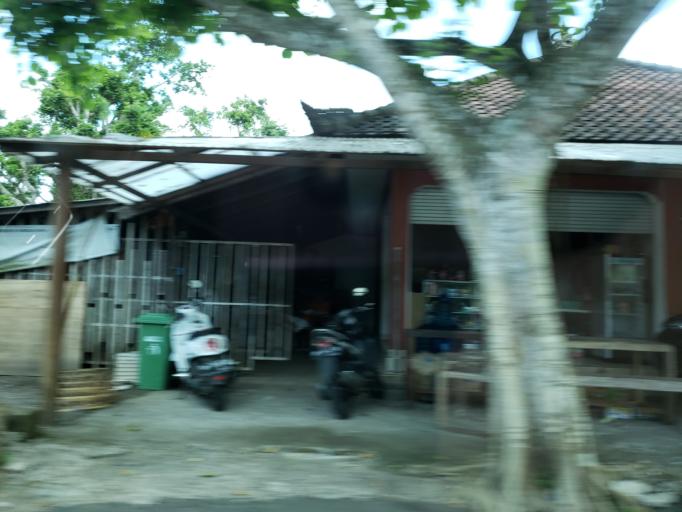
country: ID
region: Bali
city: Pecatu
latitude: -8.8405
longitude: 115.1237
